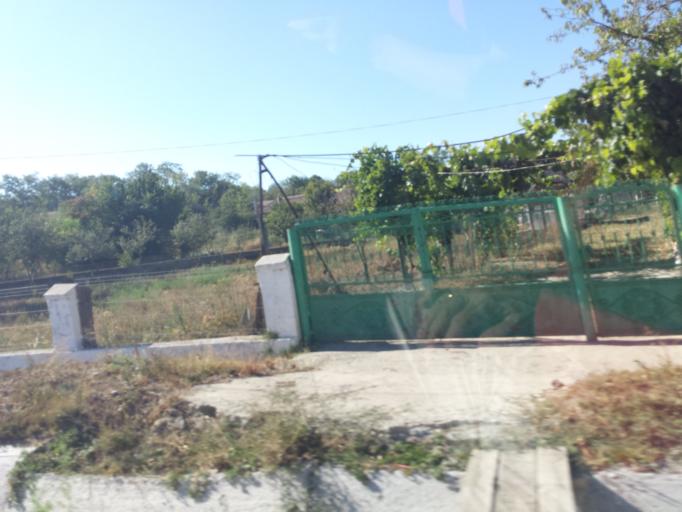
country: RO
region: Constanta
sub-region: Comuna Saraiu
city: Saraiu
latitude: 44.7215
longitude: 28.1580
